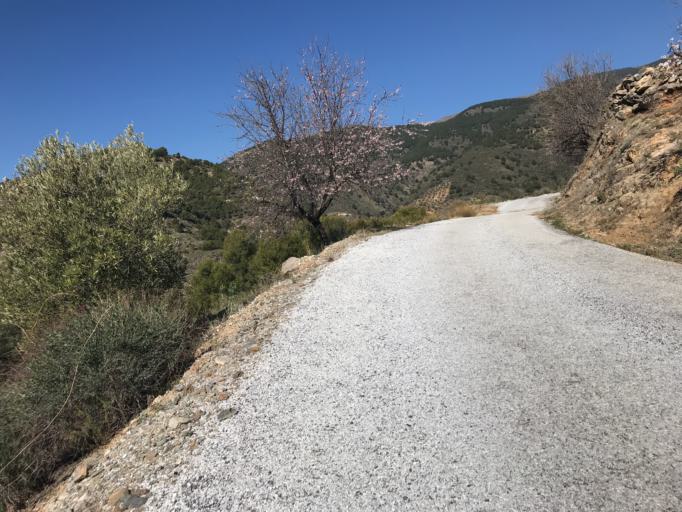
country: ES
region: Andalusia
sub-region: Provincia de Malaga
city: Canillas de Albaida
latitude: 36.8544
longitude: -3.9885
